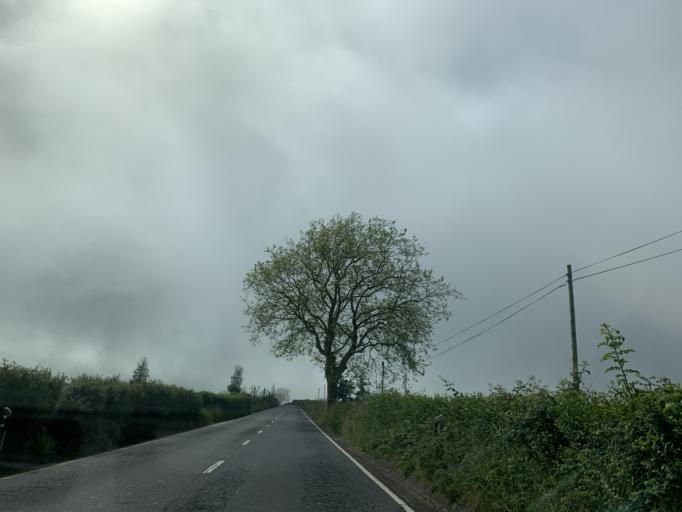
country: PT
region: Azores
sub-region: Ponta Delgada
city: Arrifes
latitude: 37.7755
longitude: -25.7485
